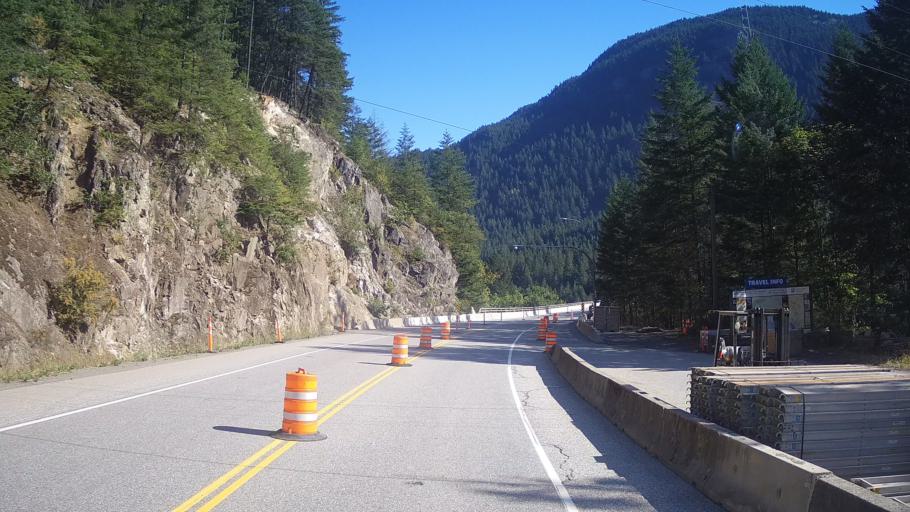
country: CA
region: British Columbia
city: Hope
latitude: 49.6982
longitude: -121.4115
